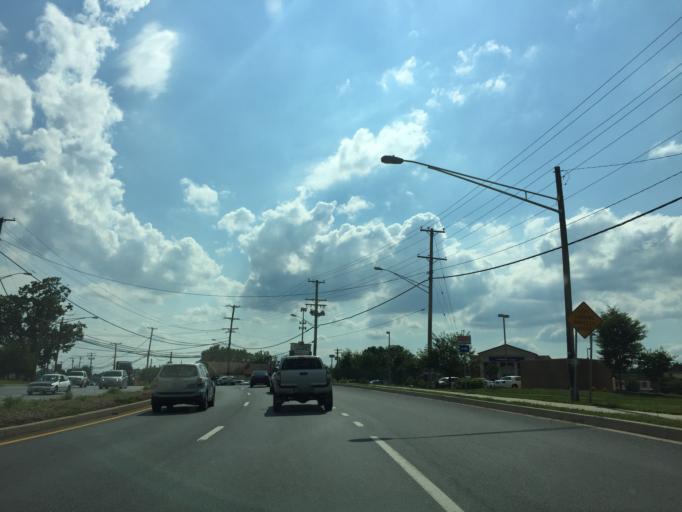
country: US
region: Maryland
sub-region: Montgomery County
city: Burtonsville
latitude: 39.1113
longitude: -76.9325
